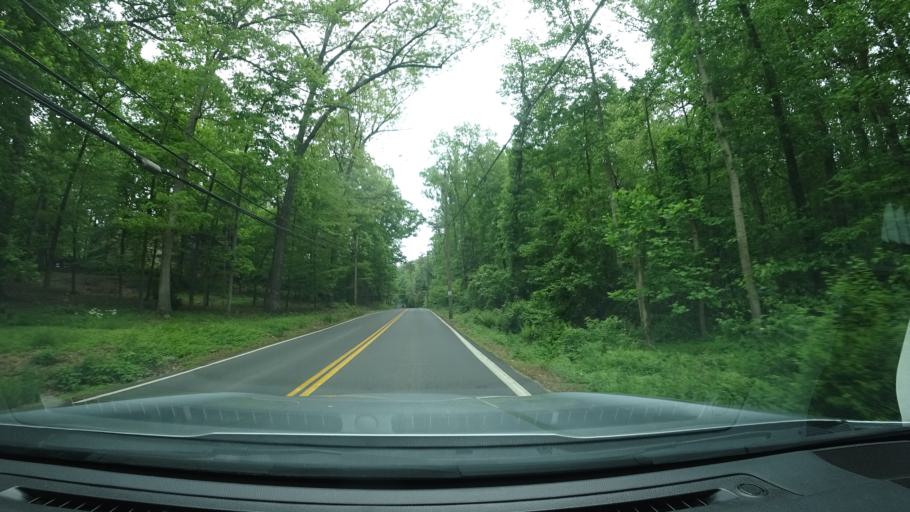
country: US
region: Virginia
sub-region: Fairfax County
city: Oakton
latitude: 38.8867
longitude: -77.3434
